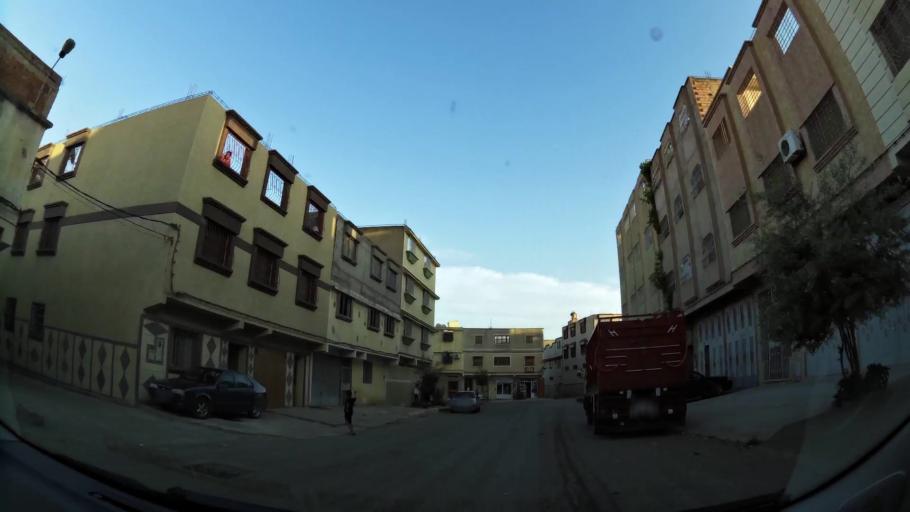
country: MA
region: Oriental
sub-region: Oujda-Angad
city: Oujda
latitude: 34.7072
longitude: -1.9110
